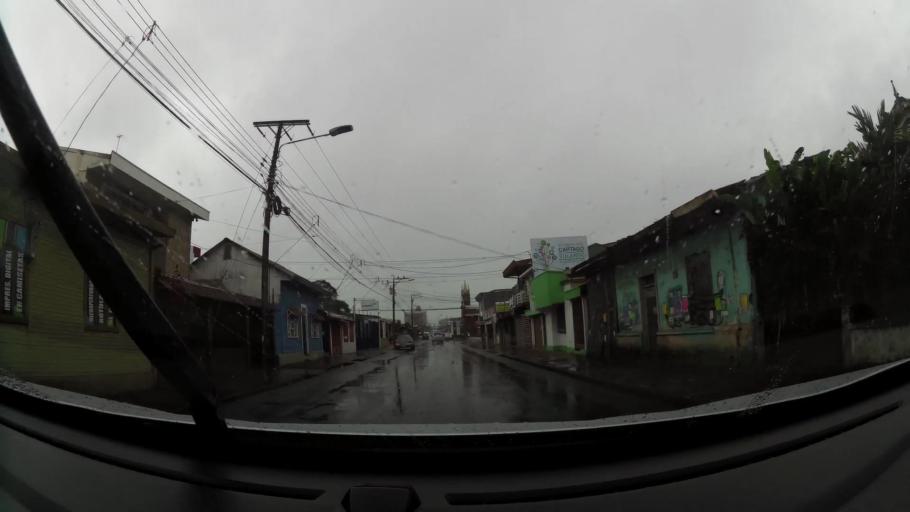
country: CR
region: Cartago
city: Cartago
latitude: 9.8658
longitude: -83.9282
